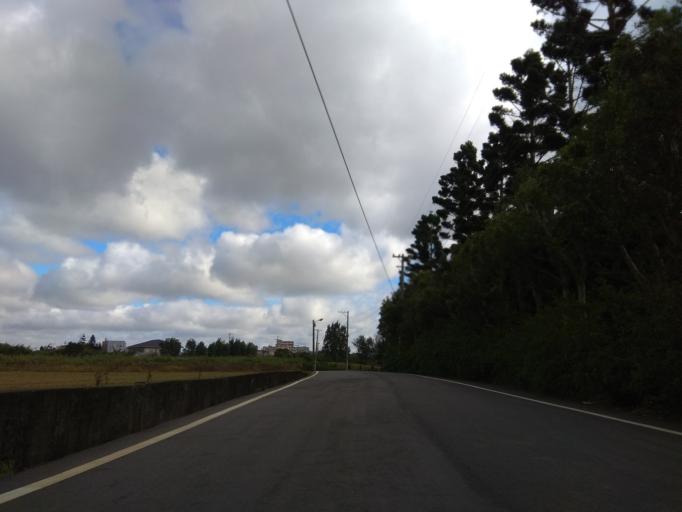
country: TW
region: Taiwan
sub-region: Hsinchu
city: Zhubei
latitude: 24.9738
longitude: 121.0847
